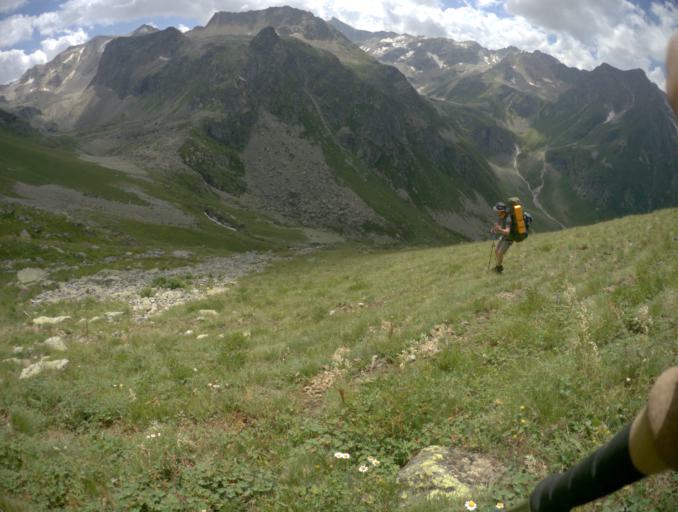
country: RU
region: Karachayevo-Cherkesiya
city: Uchkulan
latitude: 43.2949
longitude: 42.0736
